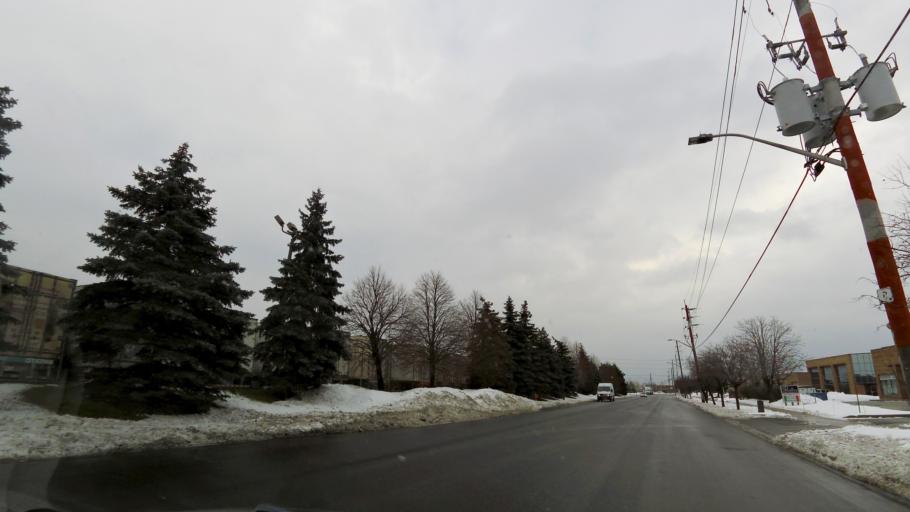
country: CA
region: Ontario
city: Mississauga
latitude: 43.6682
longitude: -79.6682
